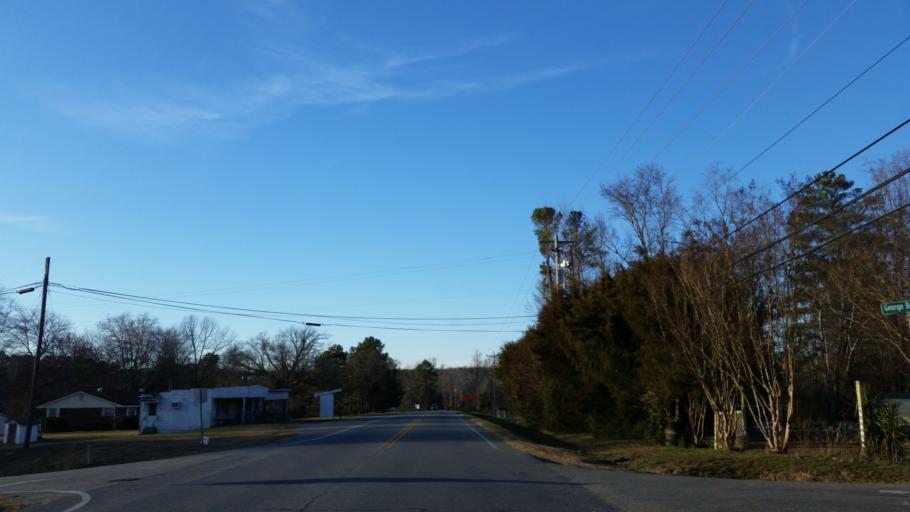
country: US
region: Georgia
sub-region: Whitfield County
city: Dalton
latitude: 34.6447
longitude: -84.9690
